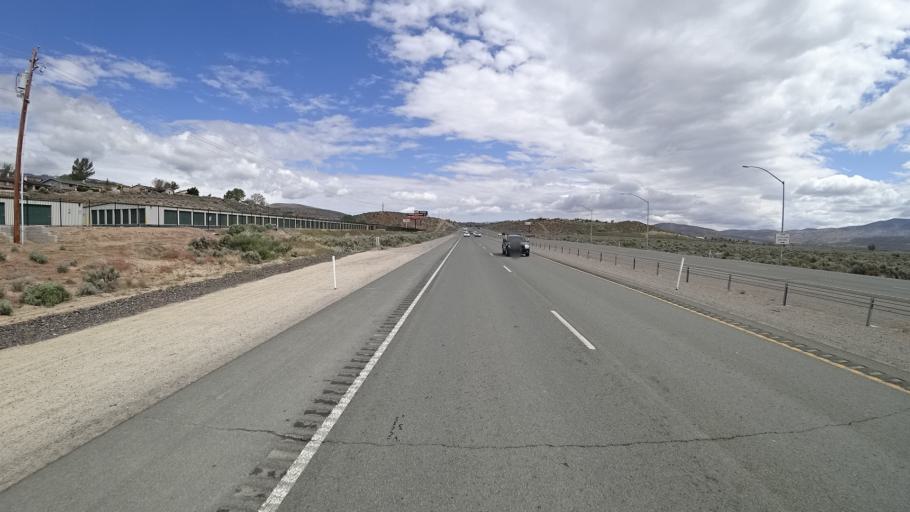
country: US
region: Nevada
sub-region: Douglas County
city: Indian Hills
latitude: 39.0769
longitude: -119.7787
